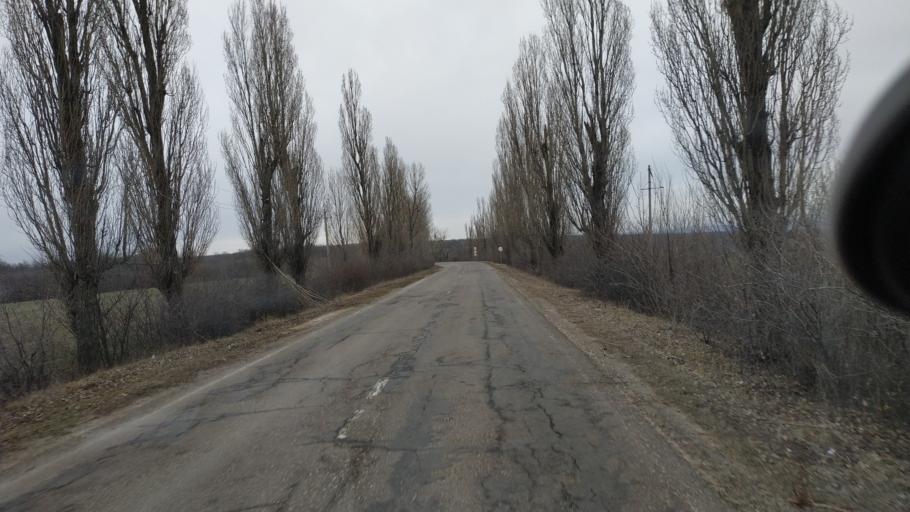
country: MD
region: Telenesti
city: Cocieri
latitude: 47.3803
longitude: 29.0432
